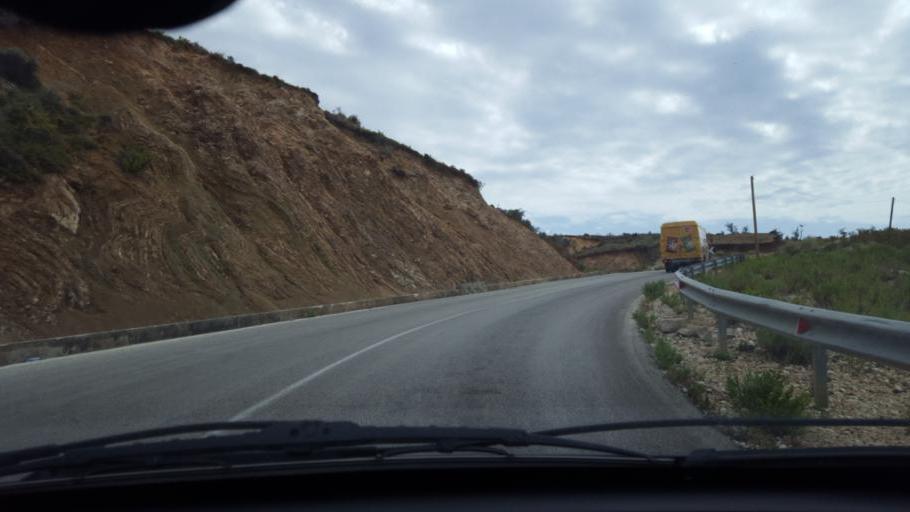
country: AL
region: Vlore
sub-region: Rrethi i Sarandes
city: Lukove
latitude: 40.0425
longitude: 19.8766
